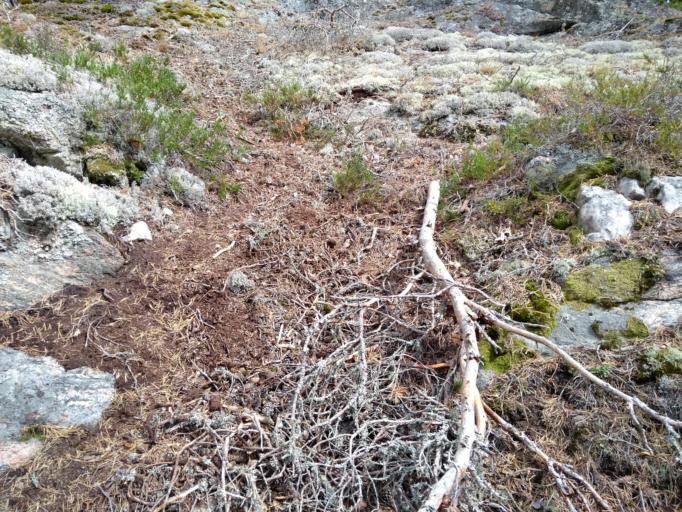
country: SE
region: OEstergoetland
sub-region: Norrkopings Kommun
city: Krokek
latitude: 58.6936
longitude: 16.5206
